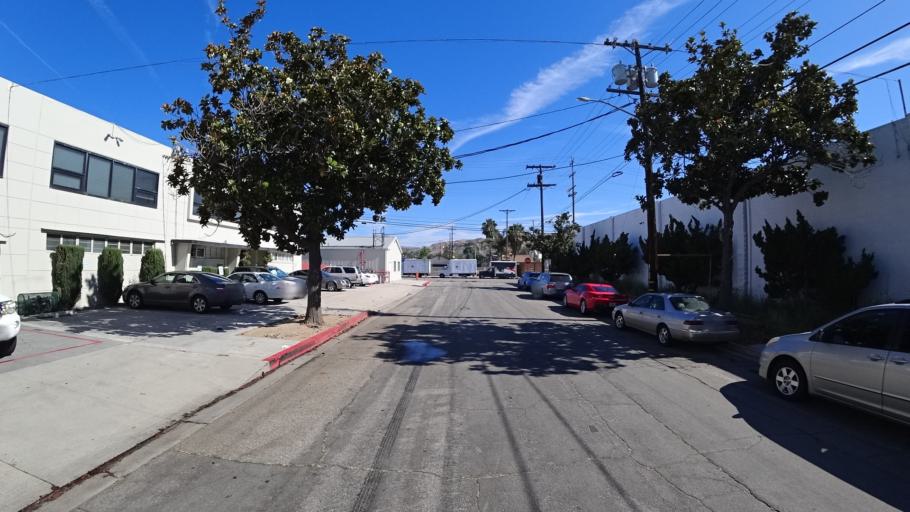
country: US
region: California
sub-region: Los Angeles County
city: North Hollywood
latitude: 34.2062
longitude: -118.3520
